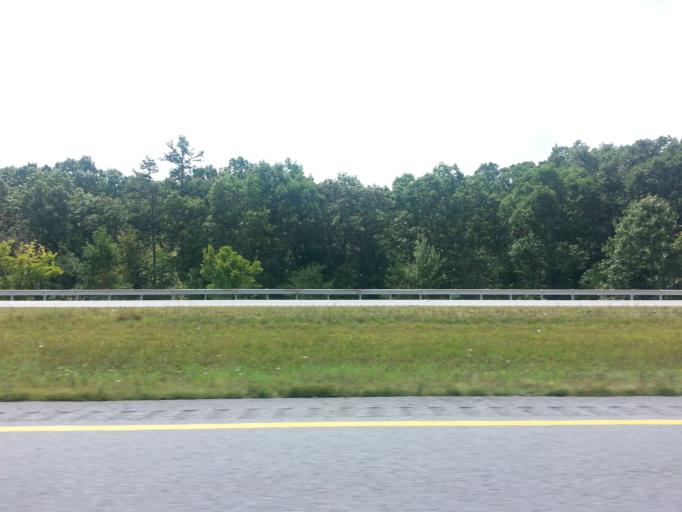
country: US
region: Tennessee
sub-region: Roane County
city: Rockwood
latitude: 35.8984
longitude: -84.7171
